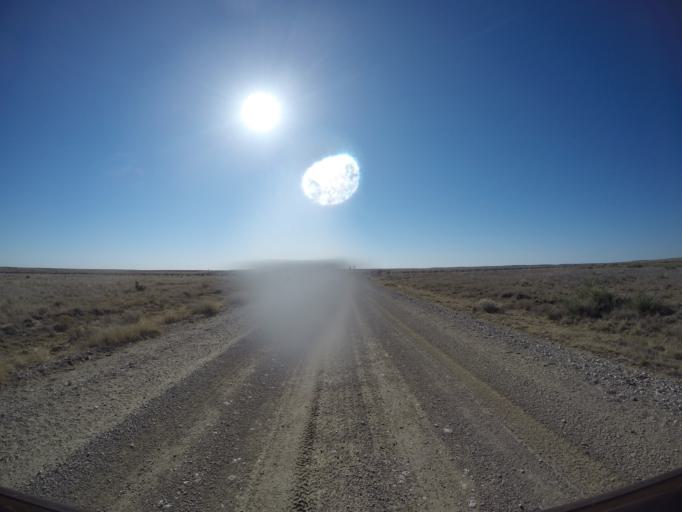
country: US
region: Colorado
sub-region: Otero County
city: La Junta
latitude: 37.7103
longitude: -103.6205
